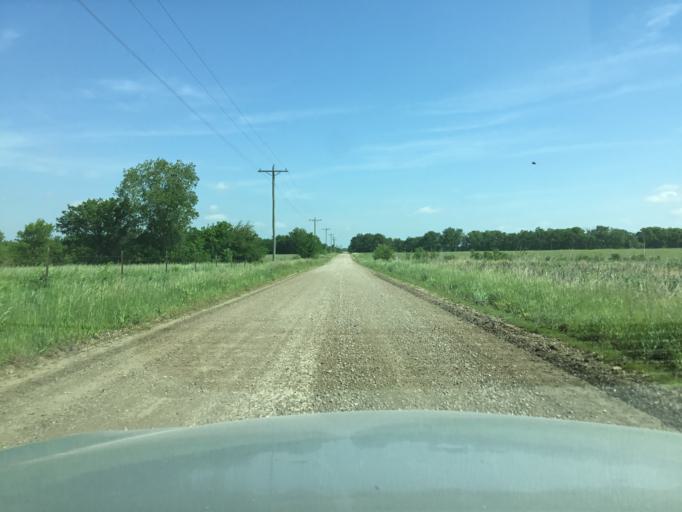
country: US
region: Kansas
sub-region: Labette County
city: Oswego
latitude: 37.1673
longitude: -95.1399
